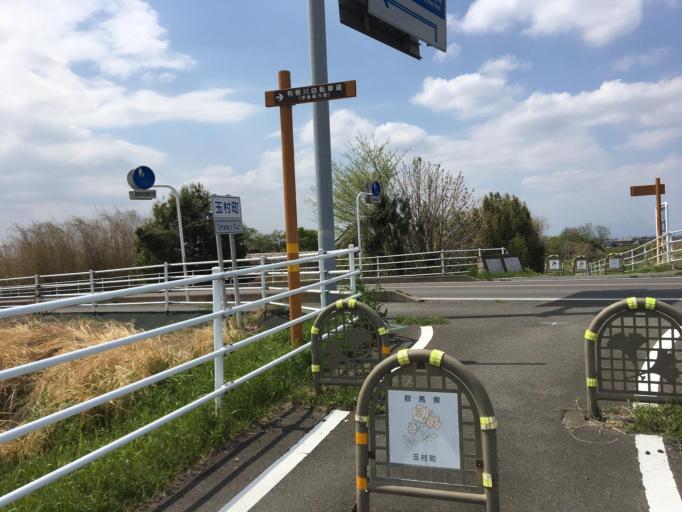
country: JP
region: Gunma
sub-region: Sawa-gun
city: Tamamura
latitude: 36.2876
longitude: 139.1607
